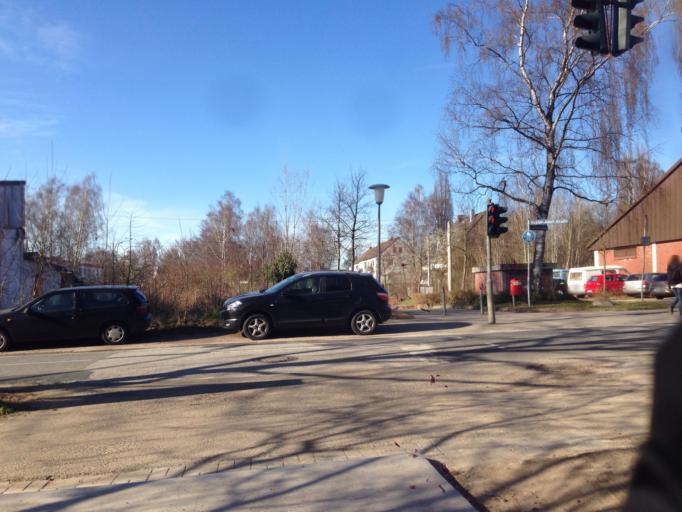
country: DE
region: Hamburg
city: Wandsbek
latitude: 53.5739
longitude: 10.0983
